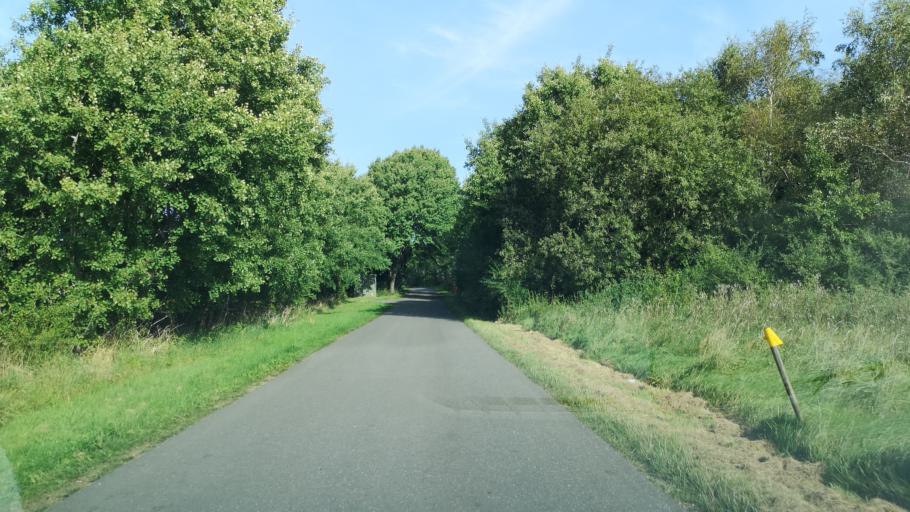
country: DK
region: Central Jutland
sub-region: Herning Kommune
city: Herning
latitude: 56.1720
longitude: 8.9582
